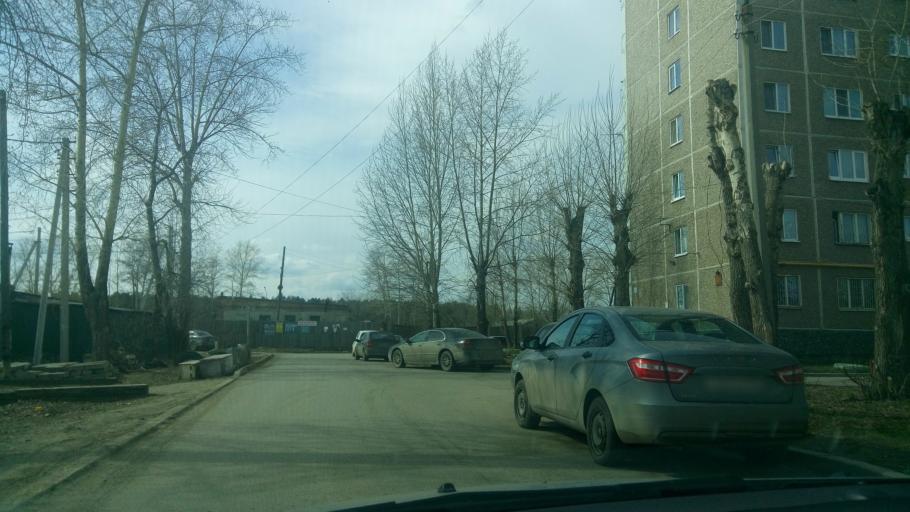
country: RU
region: Sverdlovsk
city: Verkhnyaya Pyshma
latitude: 56.9101
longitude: 60.5840
